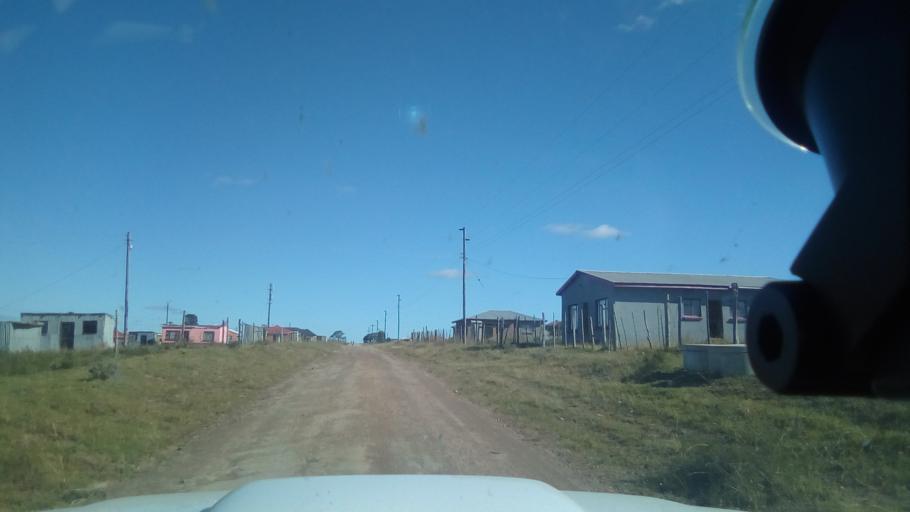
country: ZA
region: Eastern Cape
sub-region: Buffalo City Metropolitan Municipality
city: Bhisho
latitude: -32.7867
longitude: 27.3276
